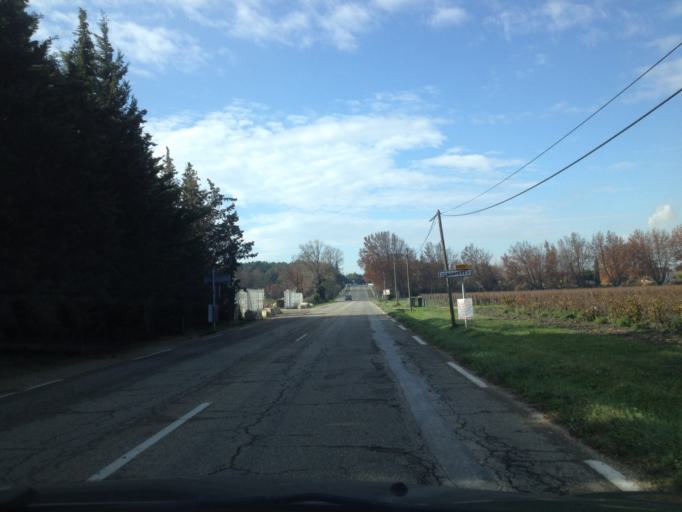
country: FR
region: Provence-Alpes-Cote d'Azur
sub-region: Departement du Vaucluse
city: Jonquieres
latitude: 44.1169
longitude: 4.8816
